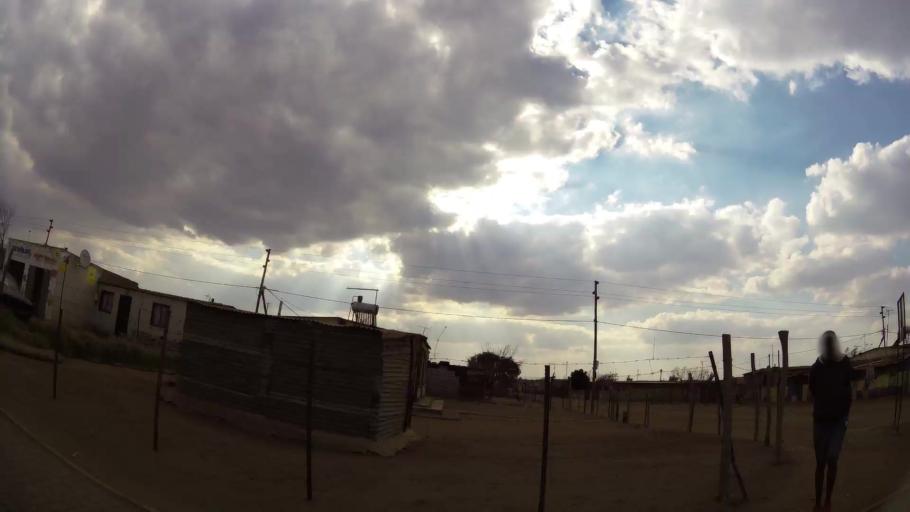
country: ZA
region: Mpumalanga
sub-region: Nkangala District Municipality
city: Delmas
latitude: -26.1399
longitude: 28.6954
